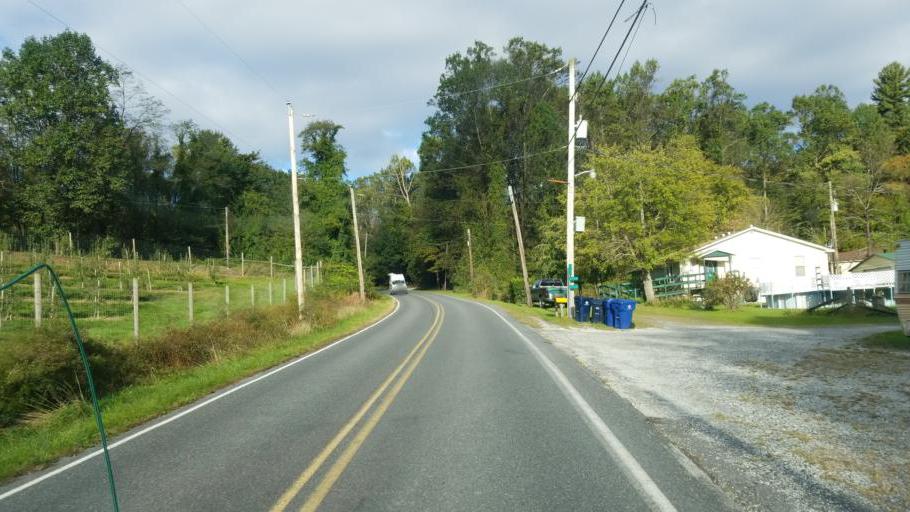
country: US
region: Pennsylvania
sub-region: Franklin County
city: Fayetteville
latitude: 39.8947
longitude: -77.4057
